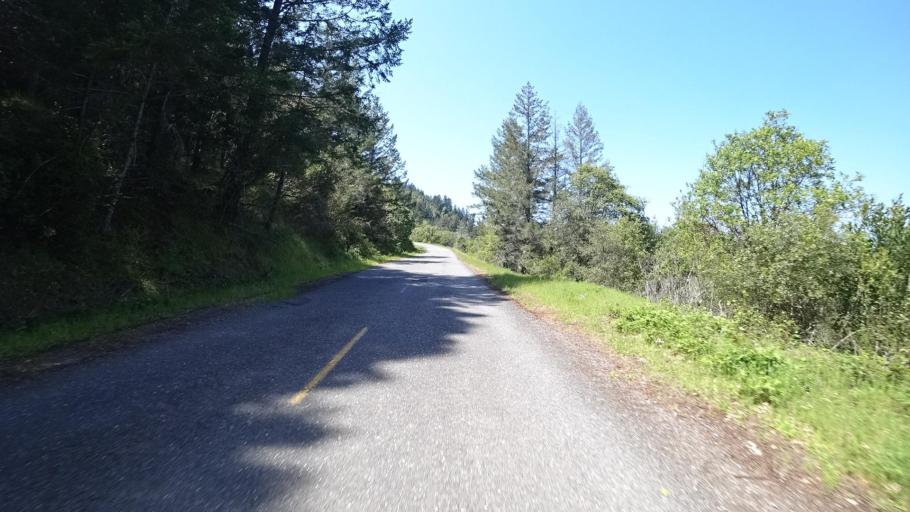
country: US
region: California
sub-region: Humboldt County
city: Redway
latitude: 40.2186
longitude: -123.6459
